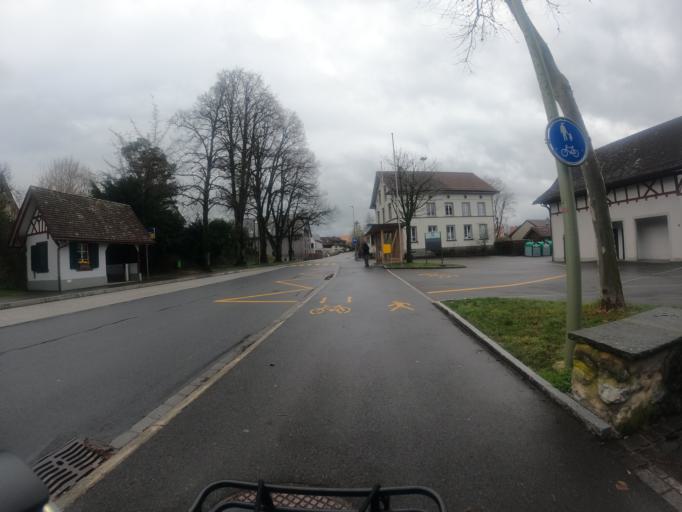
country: CH
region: Zurich
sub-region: Bezirk Affoltern
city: Hausen am Albis / Hausen (Dorf)
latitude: 47.2273
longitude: 8.5491
